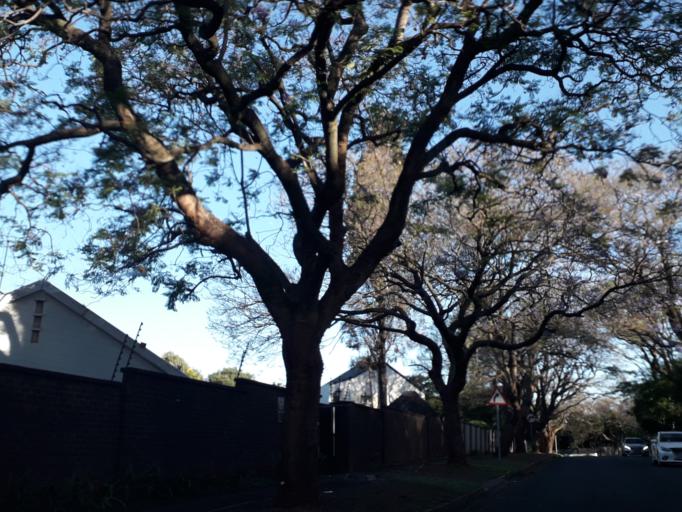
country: ZA
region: Gauteng
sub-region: City of Johannesburg Metropolitan Municipality
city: Johannesburg
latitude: -26.1675
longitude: 28.0103
